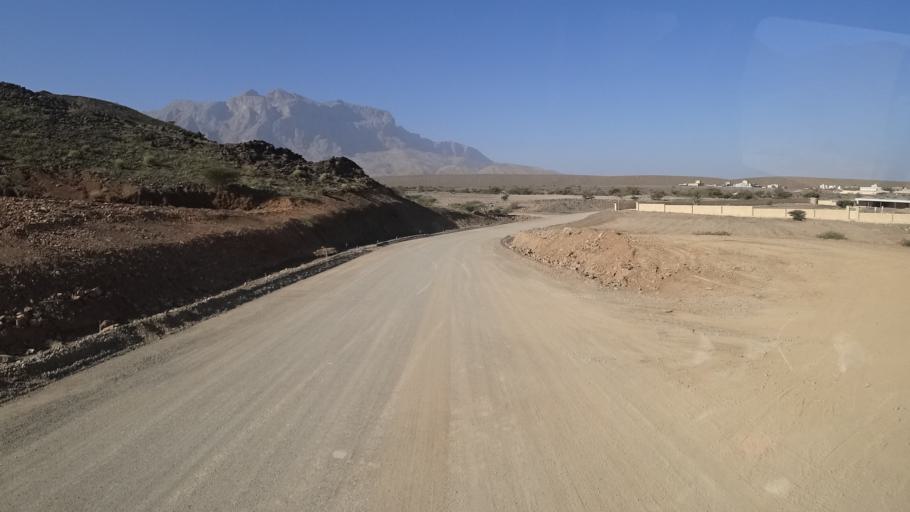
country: OM
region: Muhafazat ad Dakhiliyah
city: Bahla'
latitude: 23.2249
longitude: 57.0629
